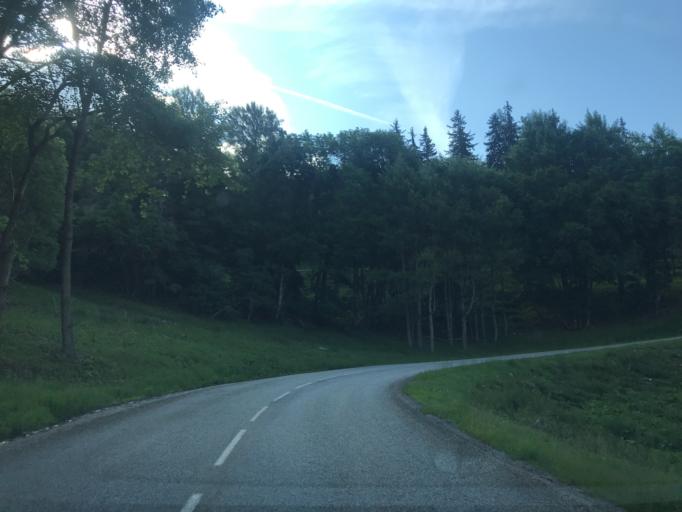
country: FR
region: Rhone-Alpes
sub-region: Departement de la Savoie
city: Modane
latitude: 45.2034
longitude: 6.6337
